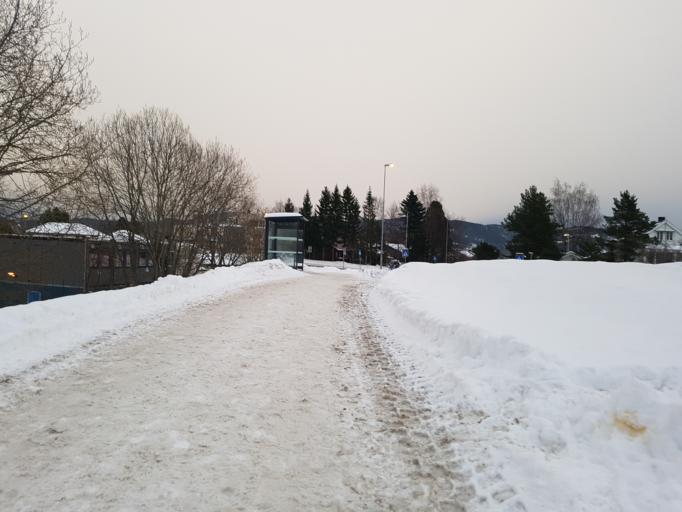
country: NO
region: Sor-Trondelag
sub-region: Trondheim
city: Trondheim
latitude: 63.3701
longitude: 10.3857
